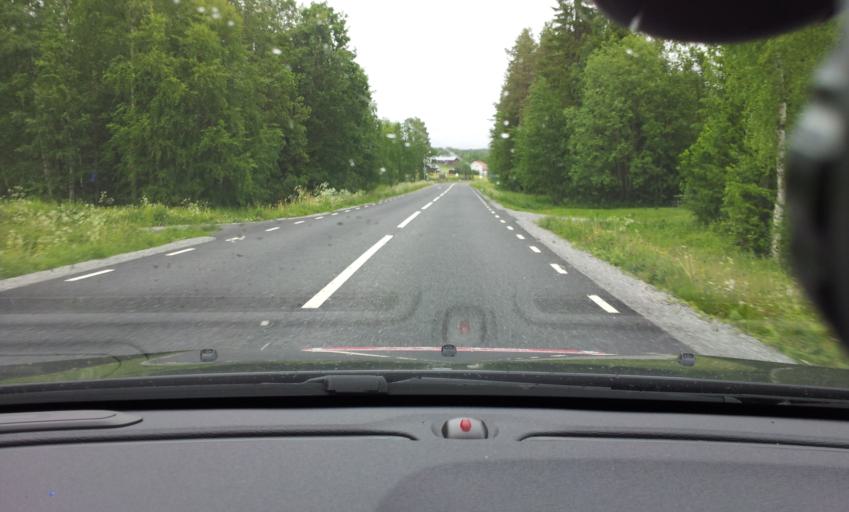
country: SE
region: Jaemtland
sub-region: OEstersunds Kommun
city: Lit
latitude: 63.7431
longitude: 14.8201
